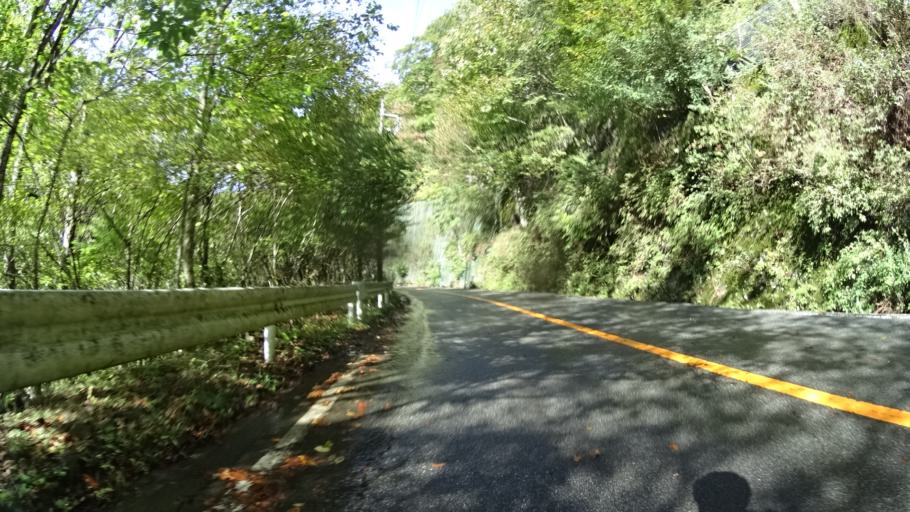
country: JP
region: Yamanashi
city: Enzan
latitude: 35.8054
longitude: 138.8491
